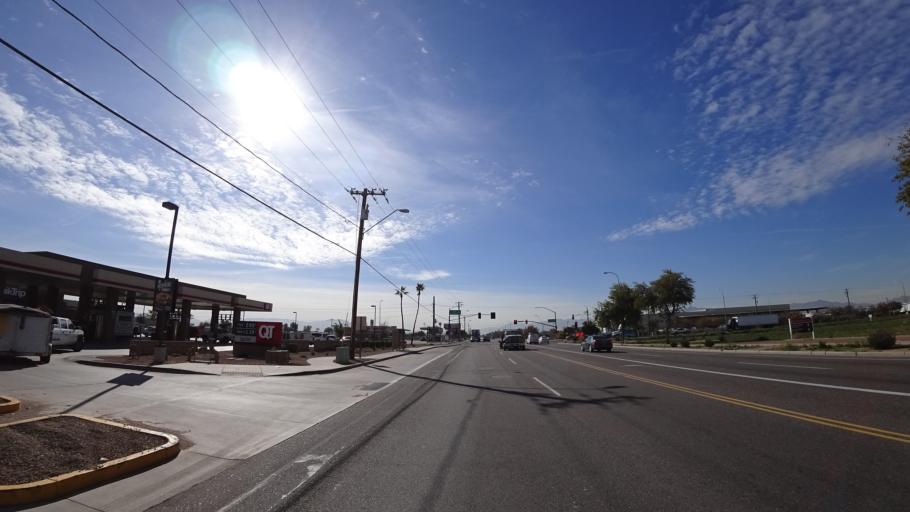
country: US
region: Arizona
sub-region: Maricopa County
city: Laveen
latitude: 33.4230
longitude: -112.1692
